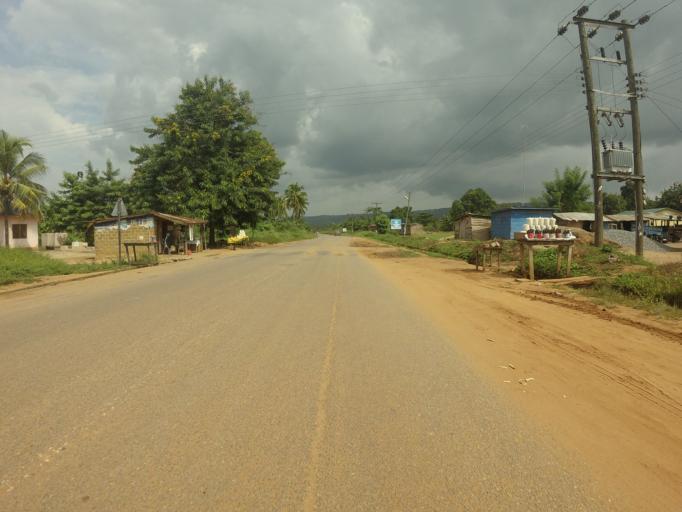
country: GH
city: Akropong
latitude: 5.9546
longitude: -0.1616
